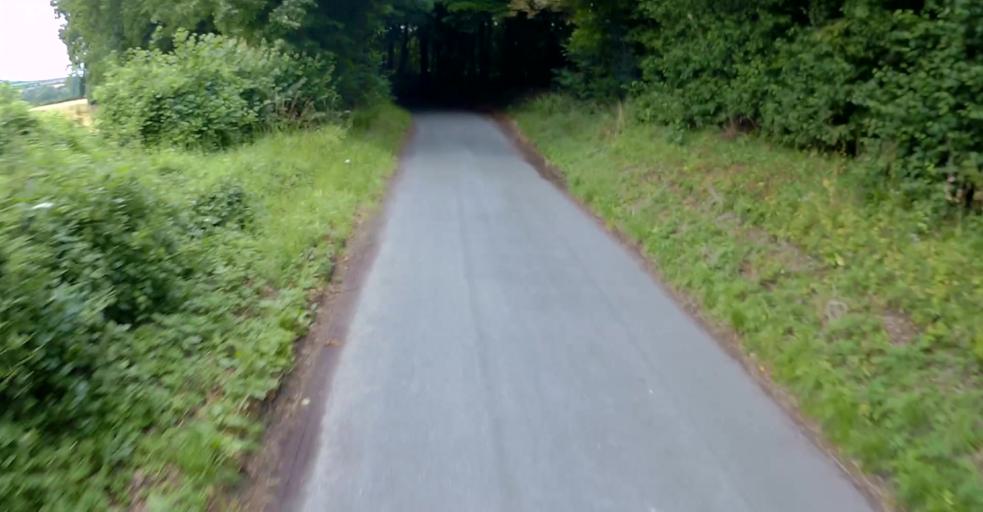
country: GB
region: England
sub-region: Hampshire
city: Kings Worthy
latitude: 51.0756
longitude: -1.2043
